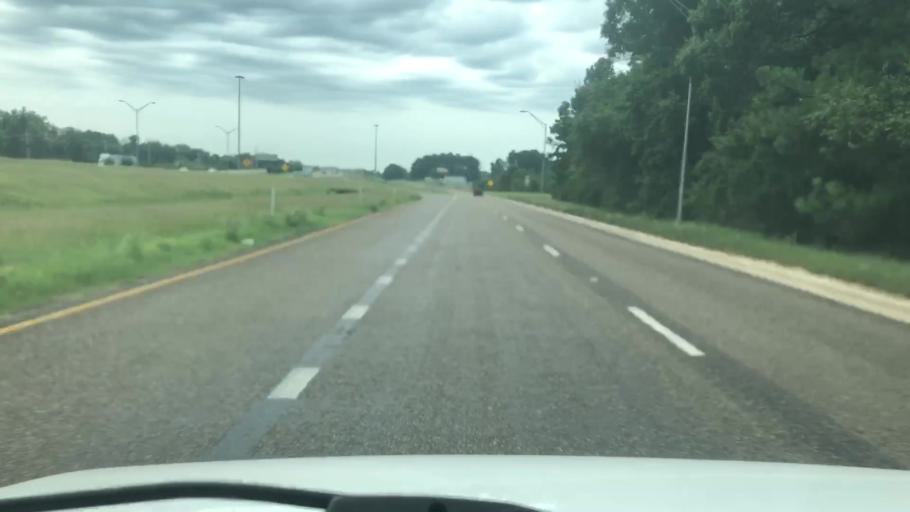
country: US
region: Texas
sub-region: Bowie County
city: Wake Village
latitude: 33.4366
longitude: -94.0974
